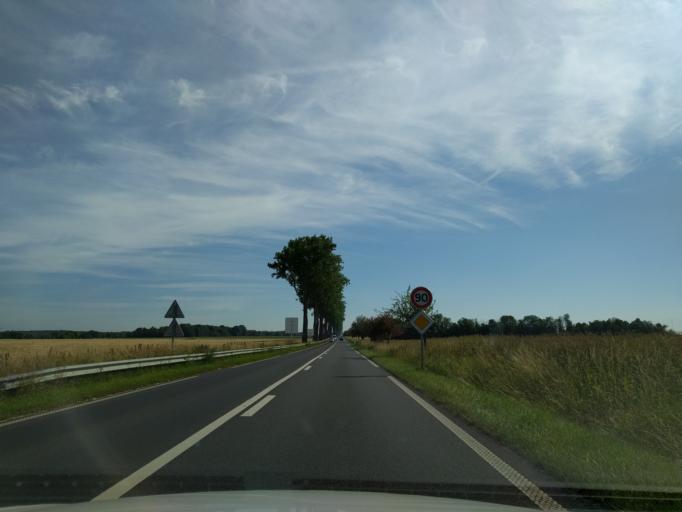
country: FR
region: Picardie
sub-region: Departement de l'Oise
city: Tille
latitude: 49.4696
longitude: 2.1193
